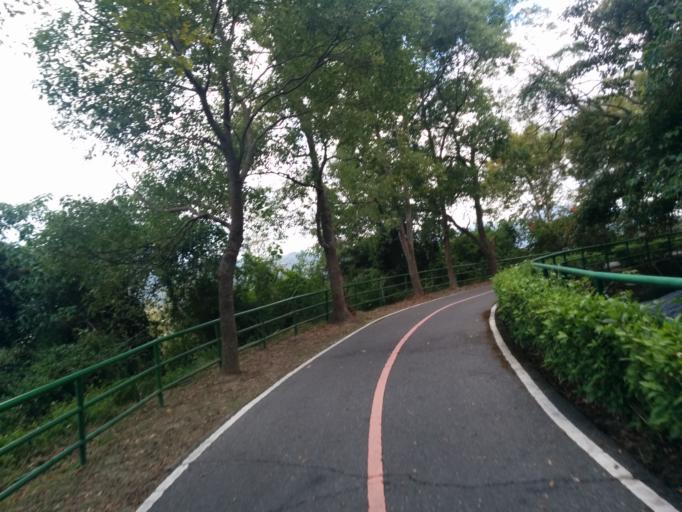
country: TW
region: Taiwan
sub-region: Taitung
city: Taitung
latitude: 23.0492
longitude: 121.1551
